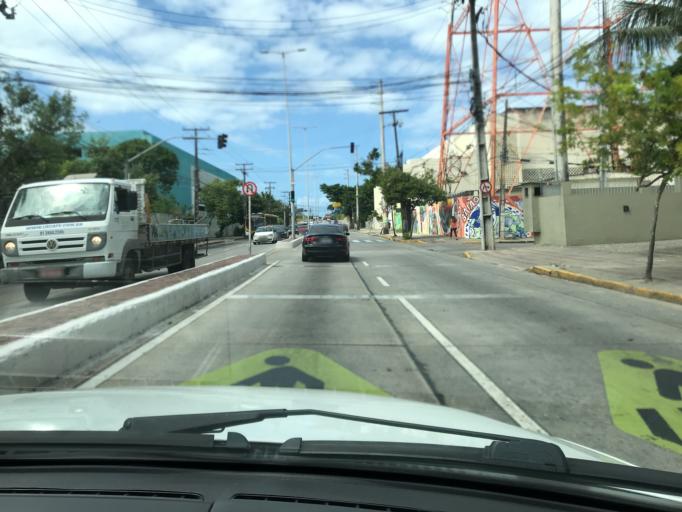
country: BR
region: Pernambuco
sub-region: Recife
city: Recife
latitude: -8.0488
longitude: -34.8753
